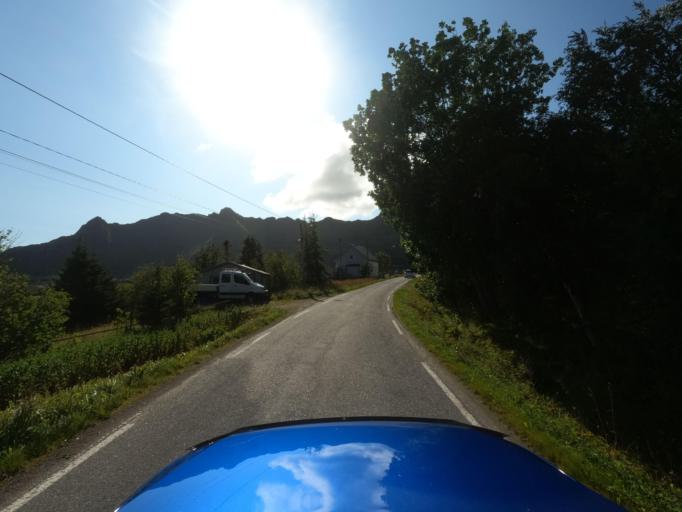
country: NO
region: Nordland
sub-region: Vestvagoy
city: Leknes
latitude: 68.1157
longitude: 13.7112
